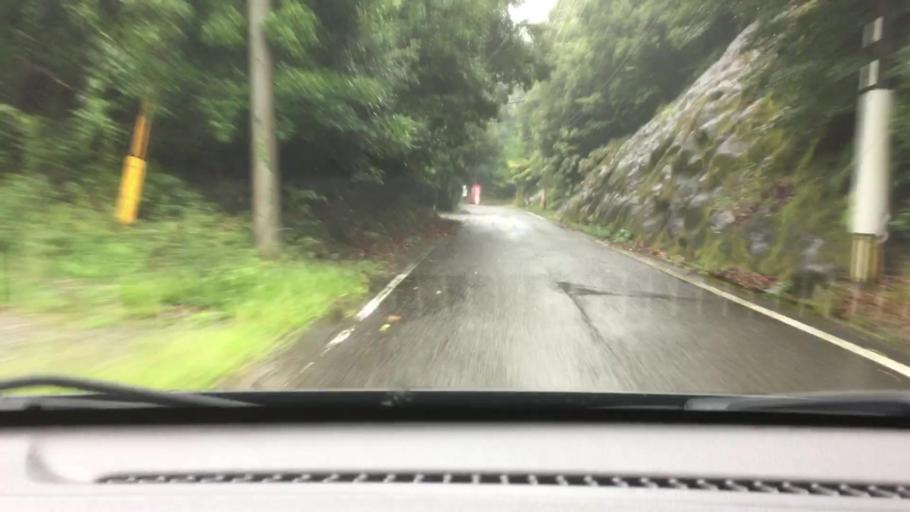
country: JP
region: Nagasaki
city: Togitsu
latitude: 32.9264
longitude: 129.7110
